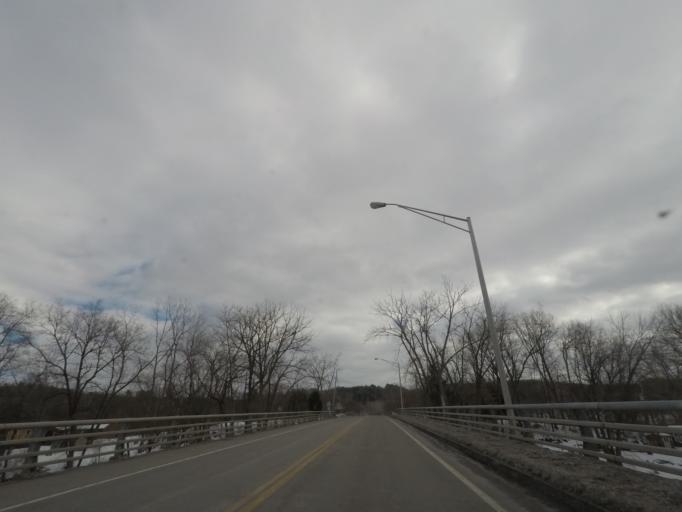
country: US
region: New York
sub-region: Saratoga County
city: Schuylerville
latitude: 43.0986
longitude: -73.5757
